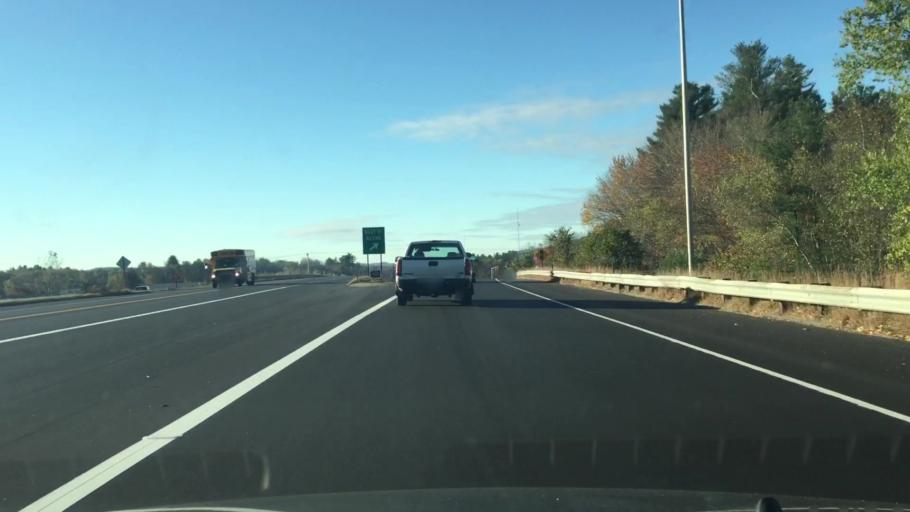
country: US
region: New Hampshire
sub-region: Cheshire County
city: Keene
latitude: 42.9363
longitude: -72.2969
